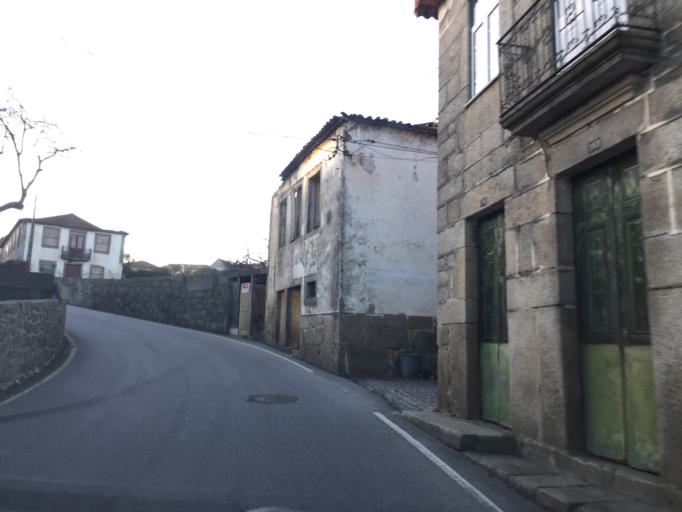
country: PT
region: Viseu
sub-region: Concelho de Carregal do Sal
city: Carregal do Sal
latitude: 40.4714
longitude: -7.9734
